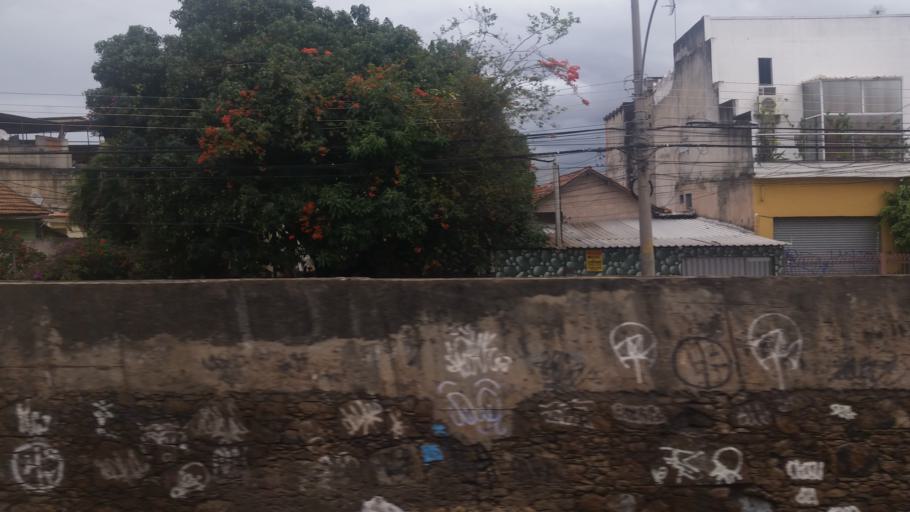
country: BR
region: Rio de Janeiro
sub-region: Sao Joao De Meriti
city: Sao Joao de Meriti
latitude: -22.8719
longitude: -43.3457
